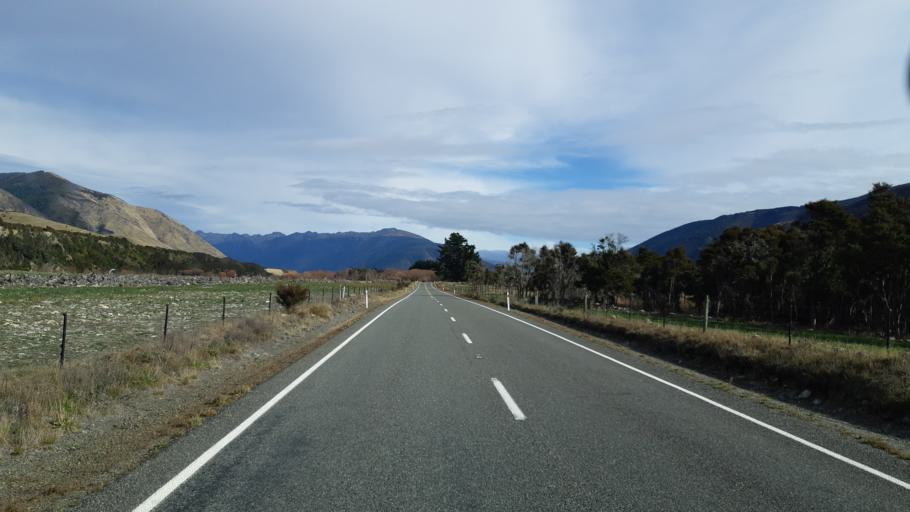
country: NZ
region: Tasman
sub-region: Tasman District
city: Wakefield
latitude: -41.7344
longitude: 173.0277
